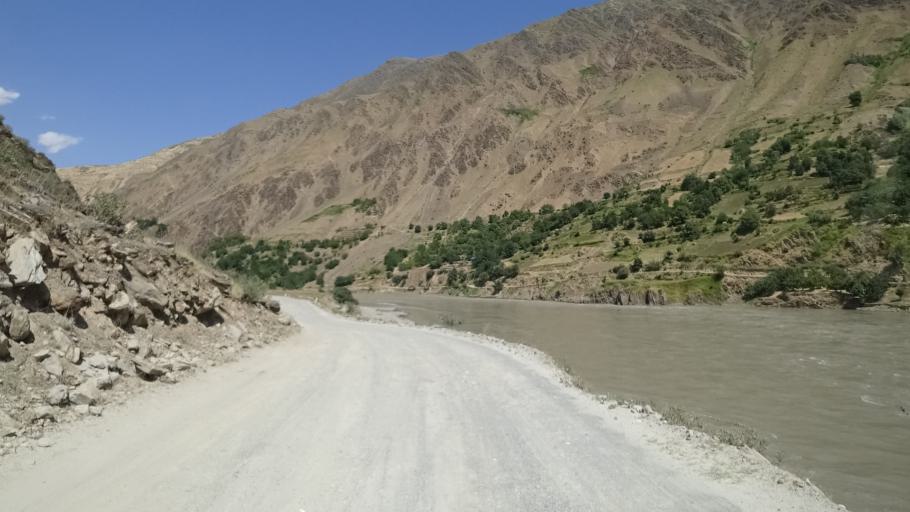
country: AF
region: Badakhshan
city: Maymay
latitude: 38.4387
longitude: 70.9532
